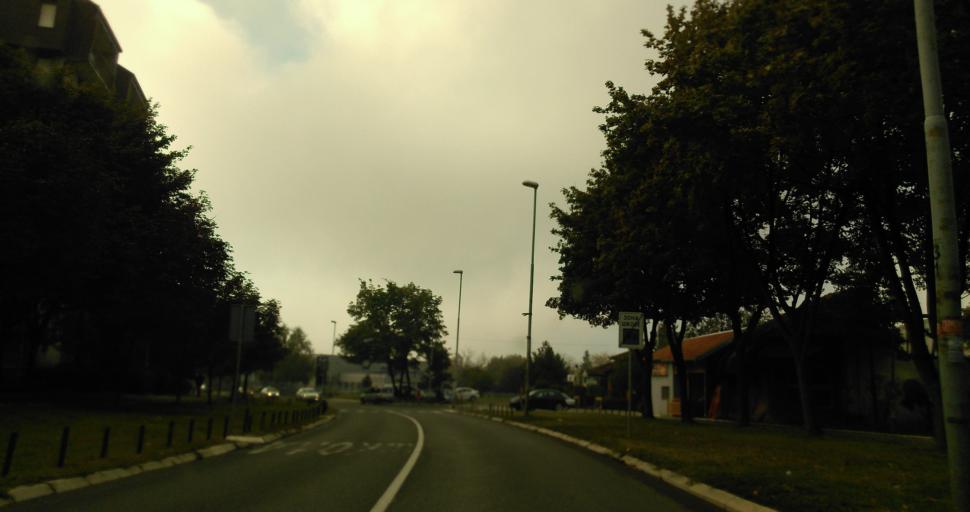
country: RS
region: Central Serbia
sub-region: Belgrade
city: Rakovica
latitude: 44.7381
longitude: 20.4197
